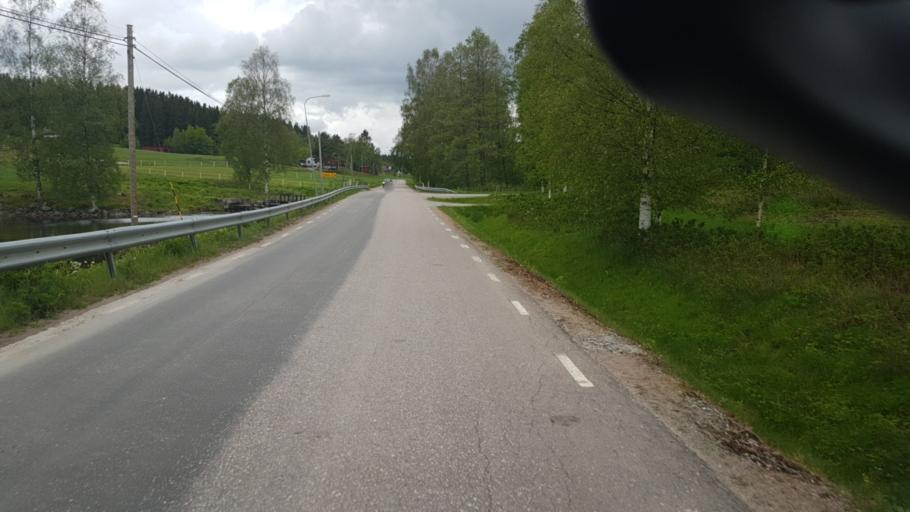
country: SE
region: Vaermland
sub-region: Arvika Kommun
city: Arvika
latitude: 59.7770
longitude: 12.7810
